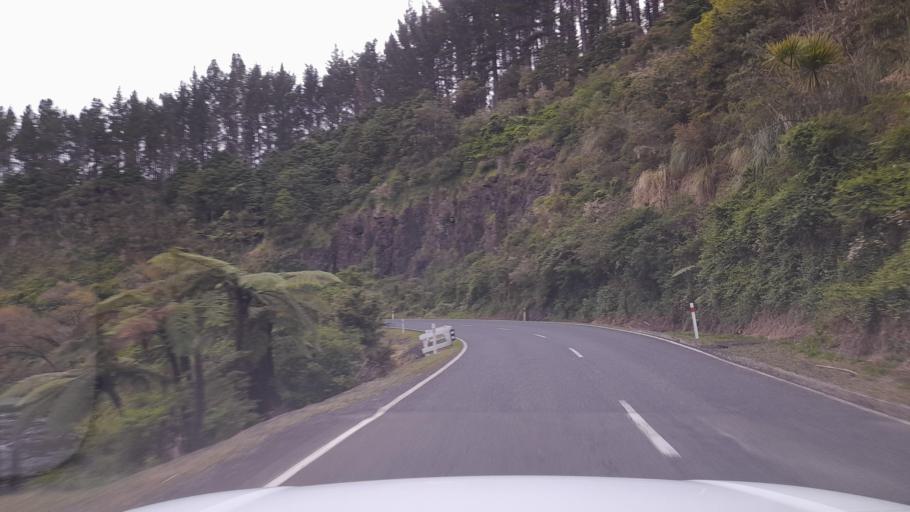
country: NZ
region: Northland
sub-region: Far North District
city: Waimate North
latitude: -35.6098
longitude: 173.8425
